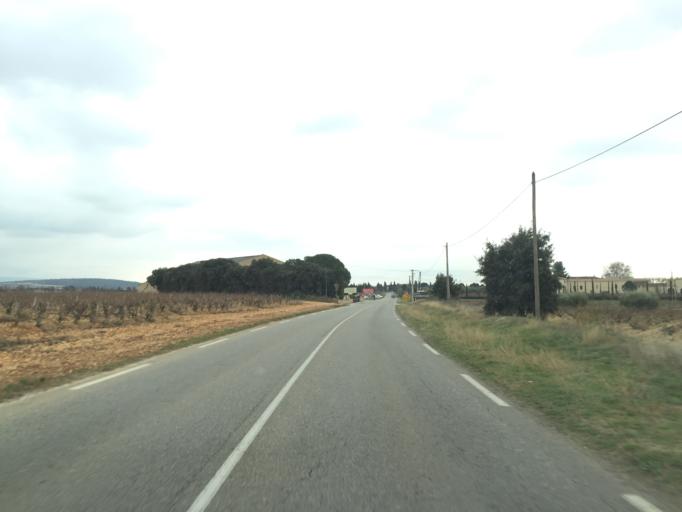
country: FR
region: Provence-Alpes-Cote d'Azur
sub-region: Departement du Vaucluse
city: Chateauneuf-du-Pape
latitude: 44.0401
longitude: 4.8526
